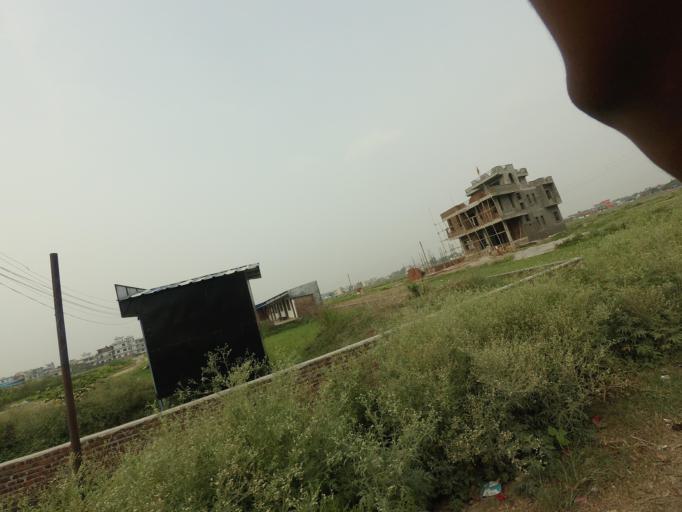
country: NP
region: Western Region
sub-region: Lumbini Zone
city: Bhairahawa
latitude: 27.5260
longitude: 83.4504
